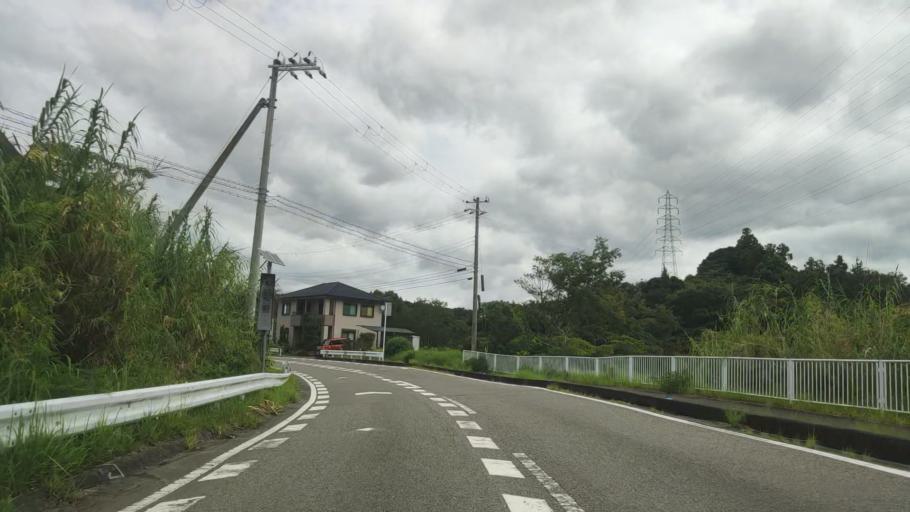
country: JP
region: Wakayama
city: Tanabe
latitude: 33.6862
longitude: 135.3885
